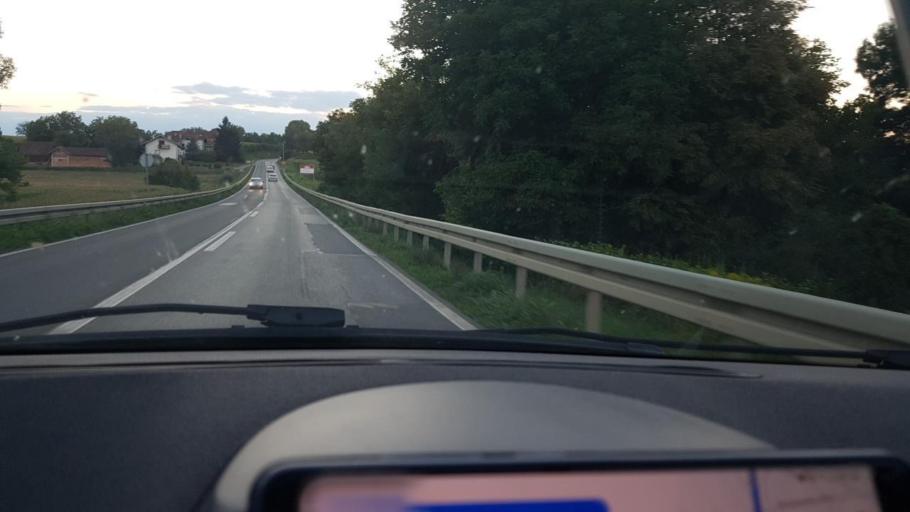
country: HR
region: Bjelovarsko-Bilogorska
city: Zdralovi
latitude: 45.8748
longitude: 16.8859
